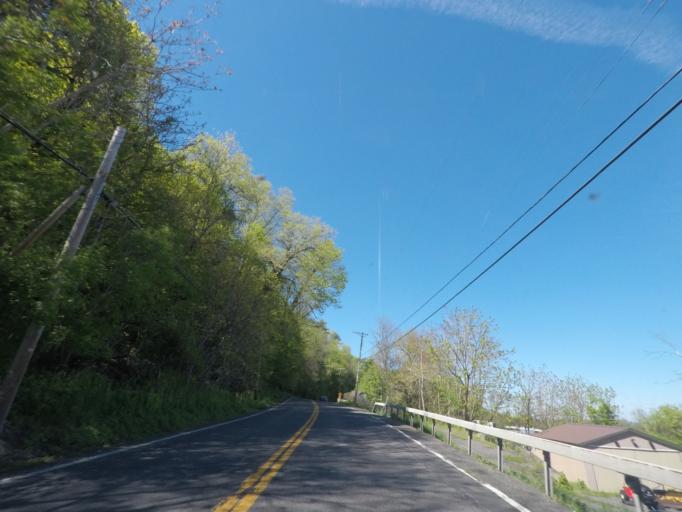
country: US
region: New York
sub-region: Ulster County
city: Saugerties
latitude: 42.1284
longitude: -73.9292
